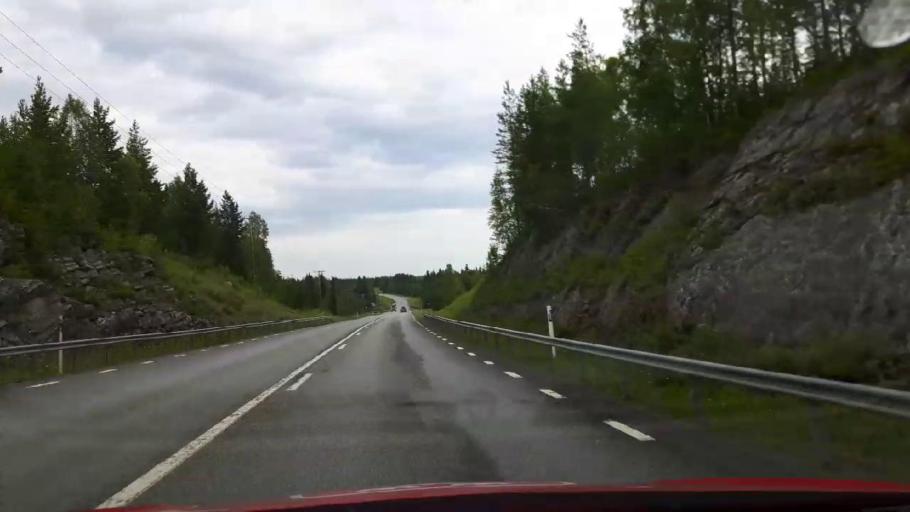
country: SE
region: Jaemtland
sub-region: Stroemsunds Kommun
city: Stroemsund
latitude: 63.6369
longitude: 15.3614
